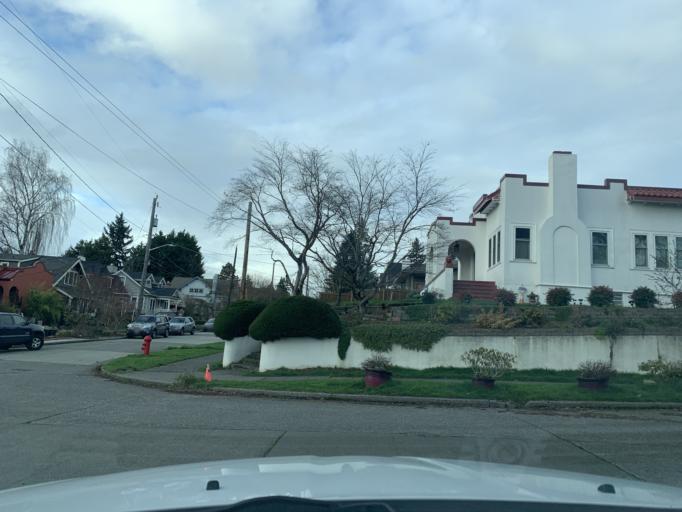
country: US
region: Washington
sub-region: King County
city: Seattle
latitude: 47.6721
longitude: -122.2961
